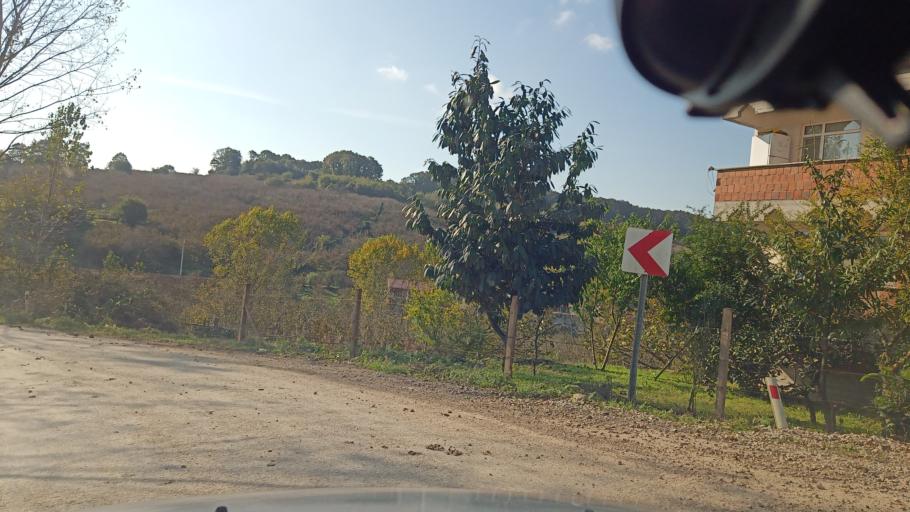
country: TR
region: Sakarya
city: Ferizli
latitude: 41.1065
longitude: 30.4756
